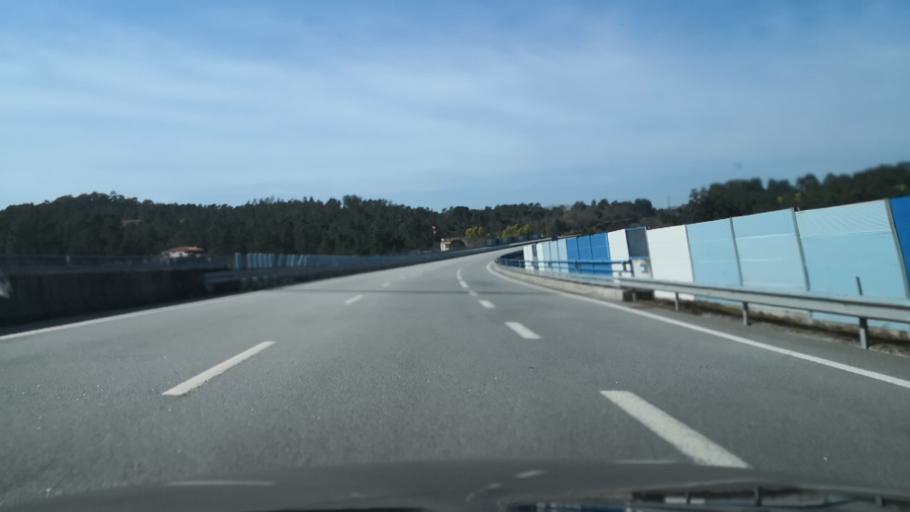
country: PT
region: Viseu
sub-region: Viseu
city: Abraveses
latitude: 40.6316
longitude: -8.0152
